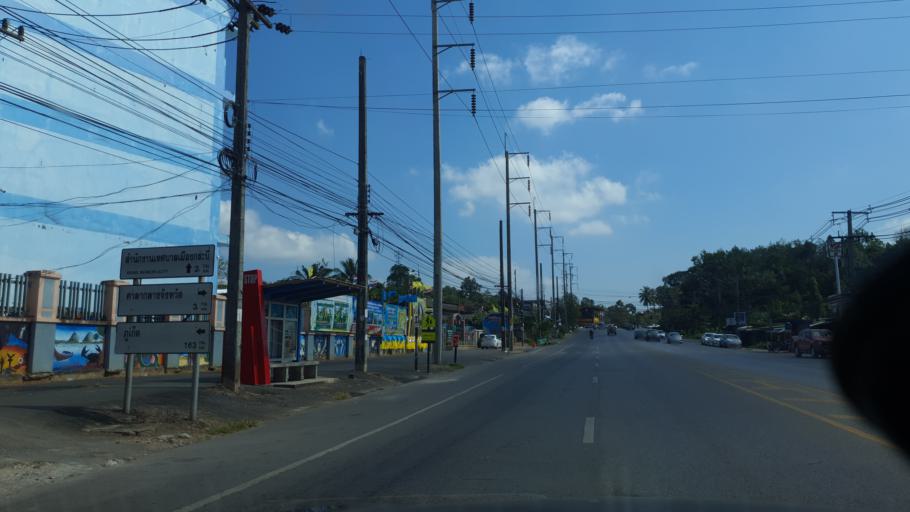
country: TH
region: Krabi
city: Krabi
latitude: 8.0829
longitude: 98.8932
